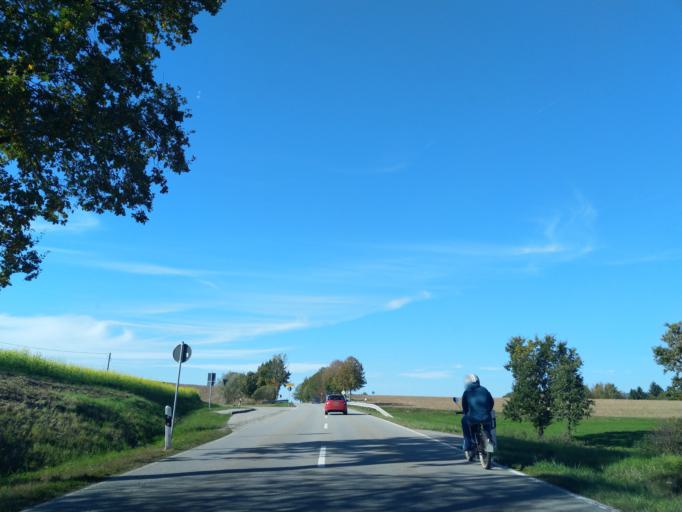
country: DE
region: Bavaria
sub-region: Lower Bavaria
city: Metten
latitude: 48.8593
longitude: 12.9402
